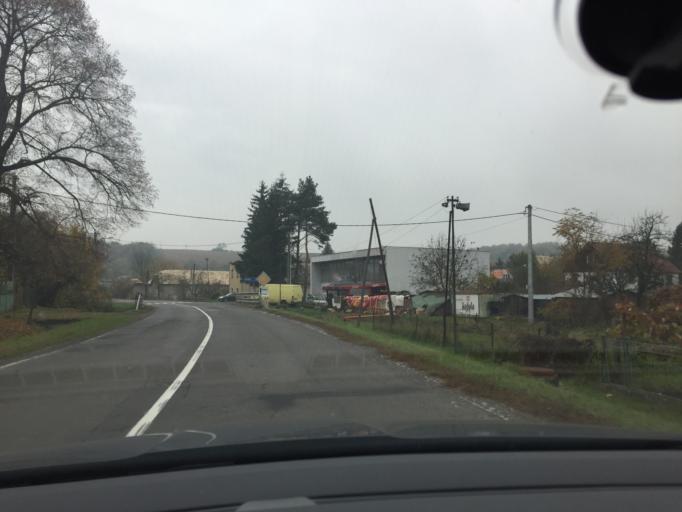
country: SK
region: Banskobystricky
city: Velky Krtis
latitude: 48.2901
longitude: 19.4886
